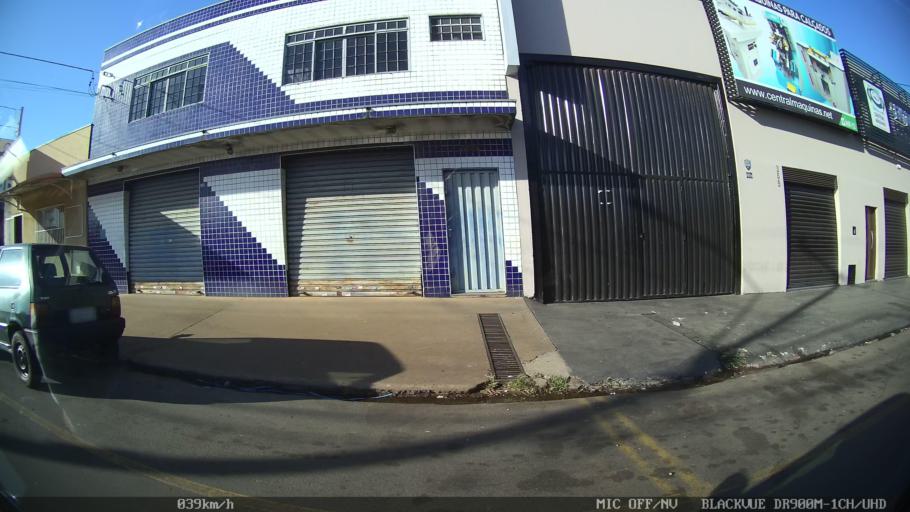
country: BR
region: Sao Paulo
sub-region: Franca
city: Franca
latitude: -20.5167
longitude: -47.3724
